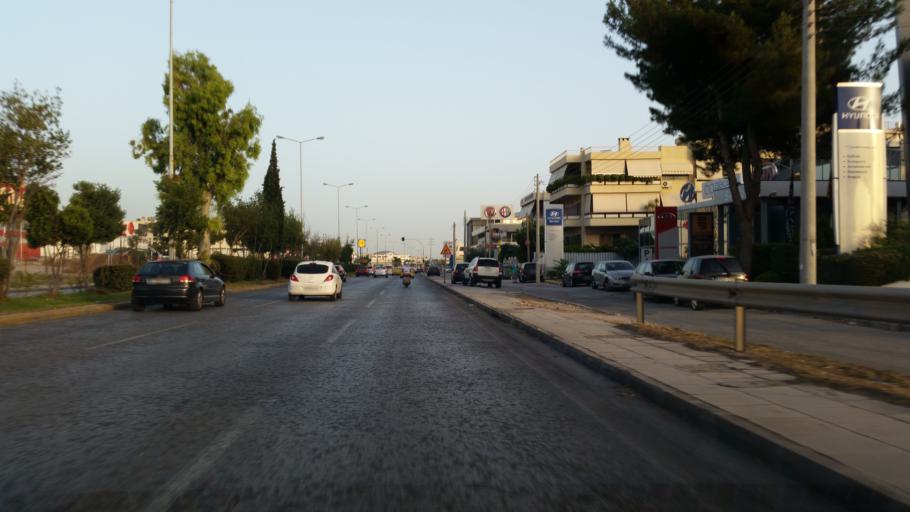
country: GR
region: Attica
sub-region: Nomarchia Athinas
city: Glyfada
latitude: 37.8736
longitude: 23.7574
